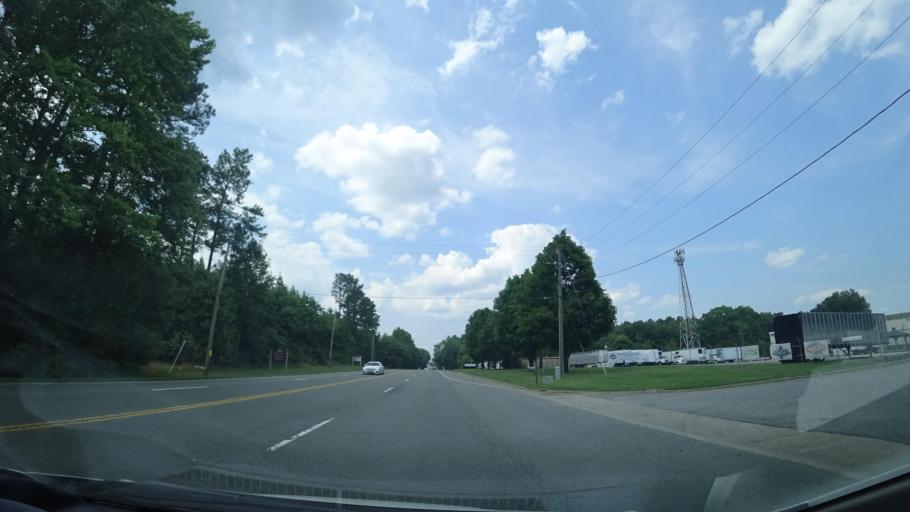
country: US
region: Virginia
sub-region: Hanover County
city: Ashland
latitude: 37.7782
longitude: -77.4664
